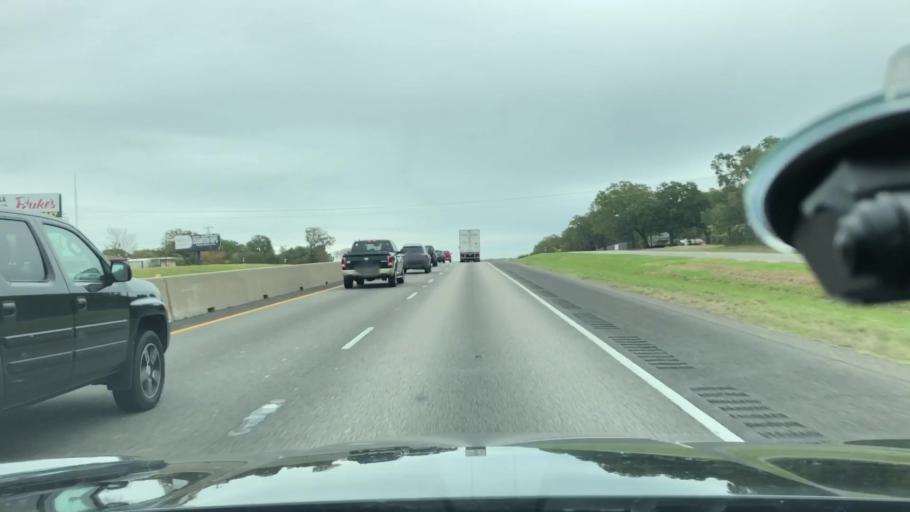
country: US
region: Texas
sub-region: Hopkins County
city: Sulphur Springs
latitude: 33.1471
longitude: -95.5417
